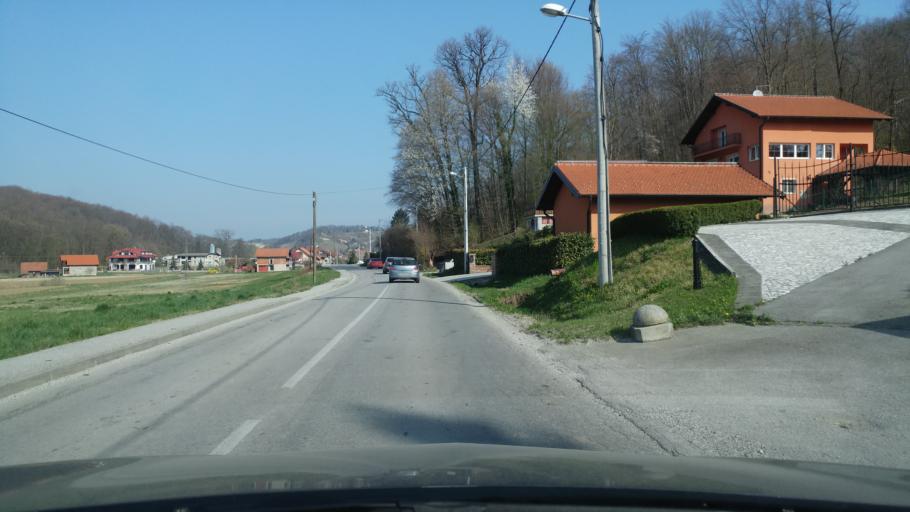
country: HR
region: Zagrebacka
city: Pojatno
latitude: 45.9034
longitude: 15.7822
